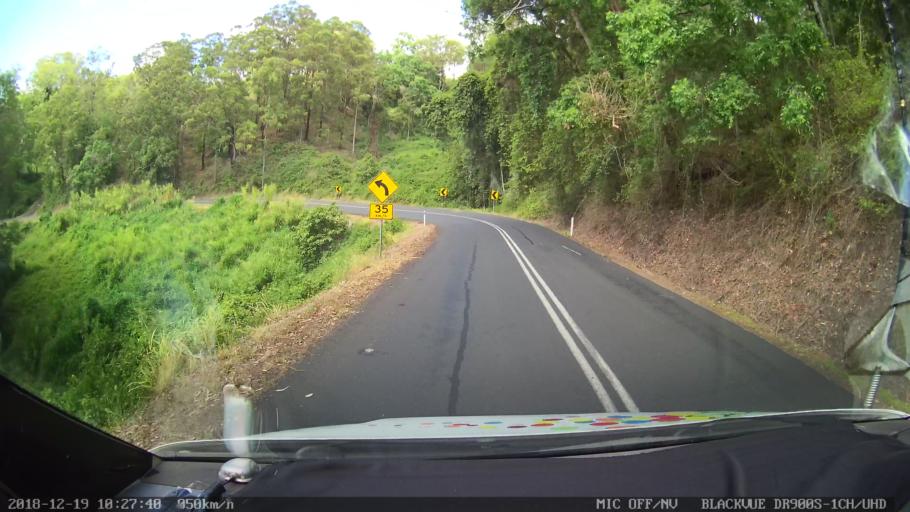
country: AU
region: New South Wales
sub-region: Lismore Municipality
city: Larnook
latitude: -28.5995
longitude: 153.0926
